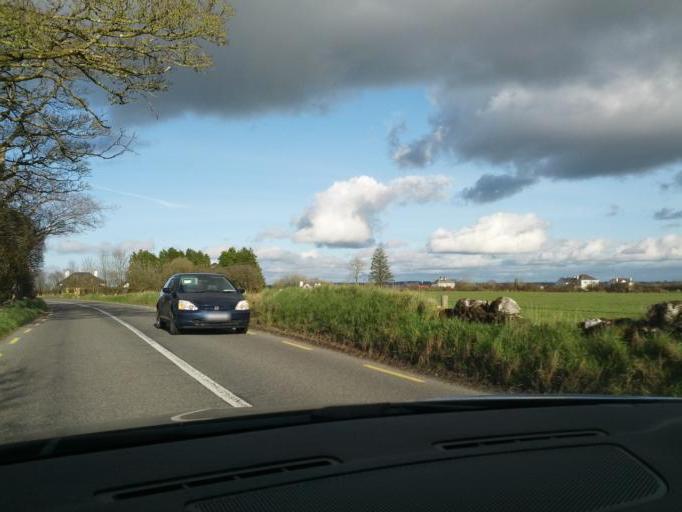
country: IE
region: Connaught
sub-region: Roscommon
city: Castlerea
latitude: 53.6877
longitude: -8.4775
